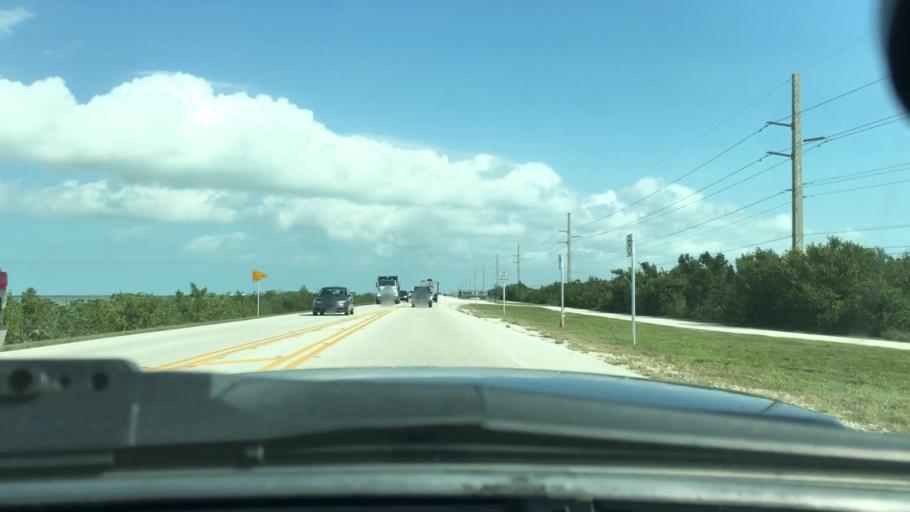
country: US
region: Florida
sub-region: Monroe County
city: Big Coppitt Key
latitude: 24.6304
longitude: -81.5910
